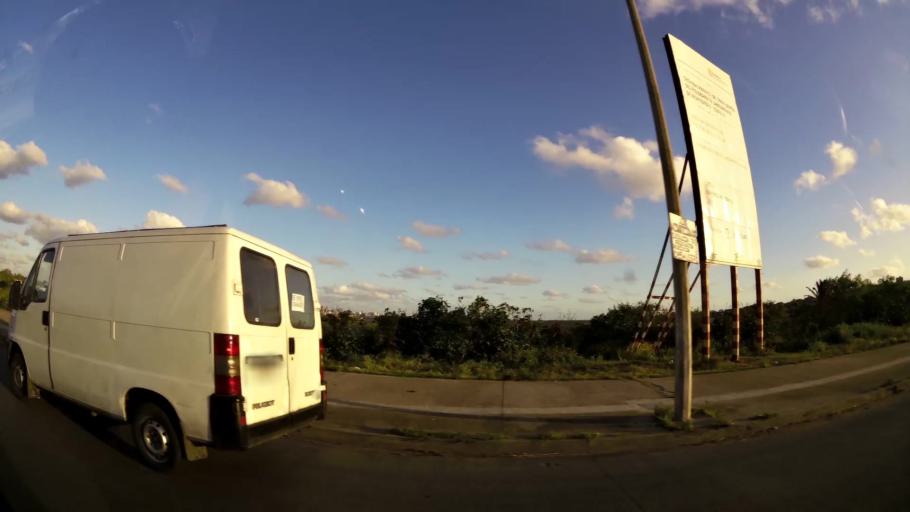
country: UY
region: Montevideo
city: Montevideo
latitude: -34.8745
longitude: -56.2460
